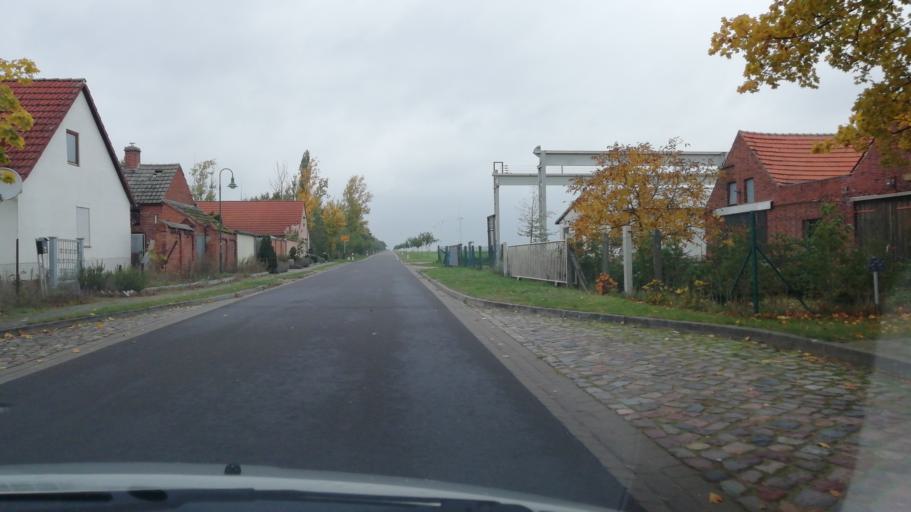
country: DE
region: Saxony-Anhalt
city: Luderitz
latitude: 52.4972
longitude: 11.7927
